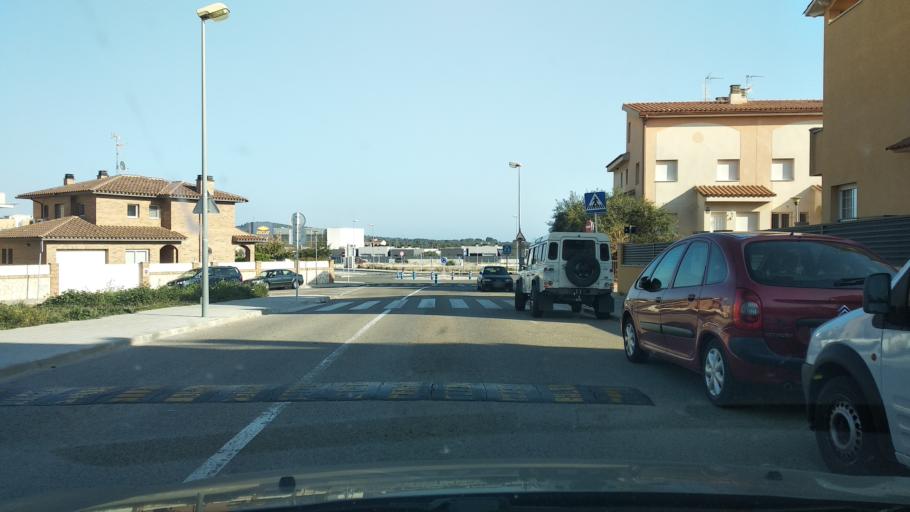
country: ES
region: Catalonia
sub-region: Provincia de Tarragona
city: El Vendrell
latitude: 41.2145
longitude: 1.5267
